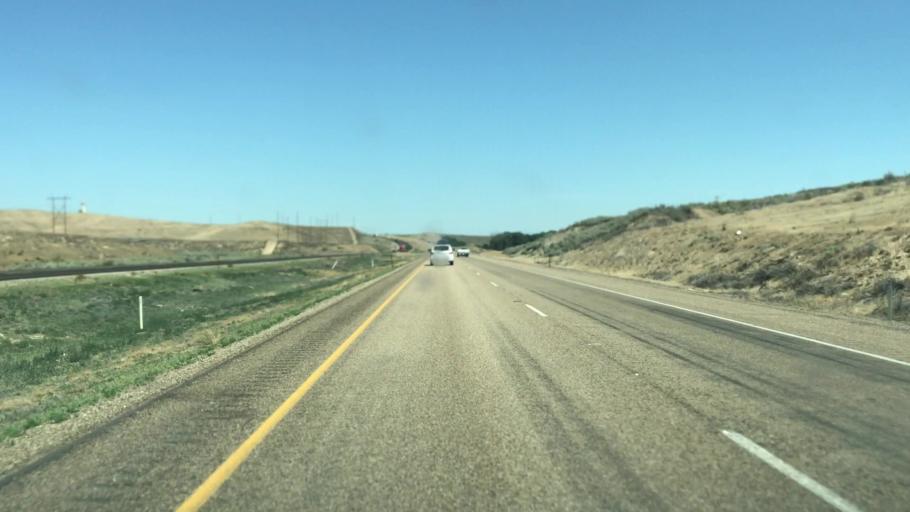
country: US
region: Idaho
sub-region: Payette County
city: New Plymouth
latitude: 43.8917
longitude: -116.8048
